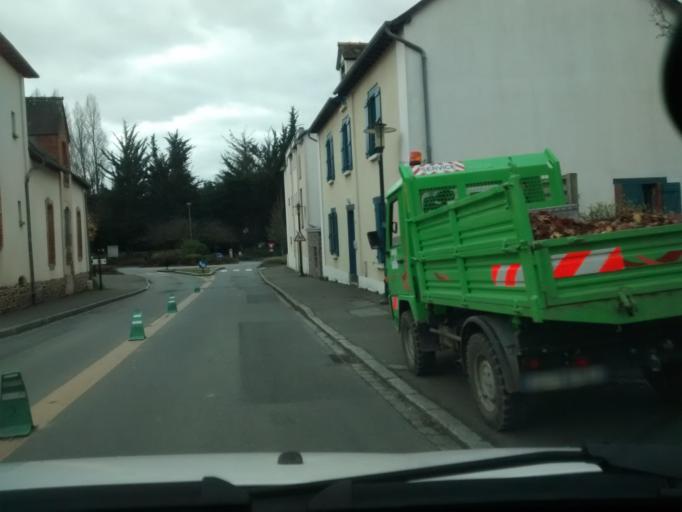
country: FR
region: Brittany
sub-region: Departement d'Ille-et-Vilaine
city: Chavagne
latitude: 48.0515
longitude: -1.7913
